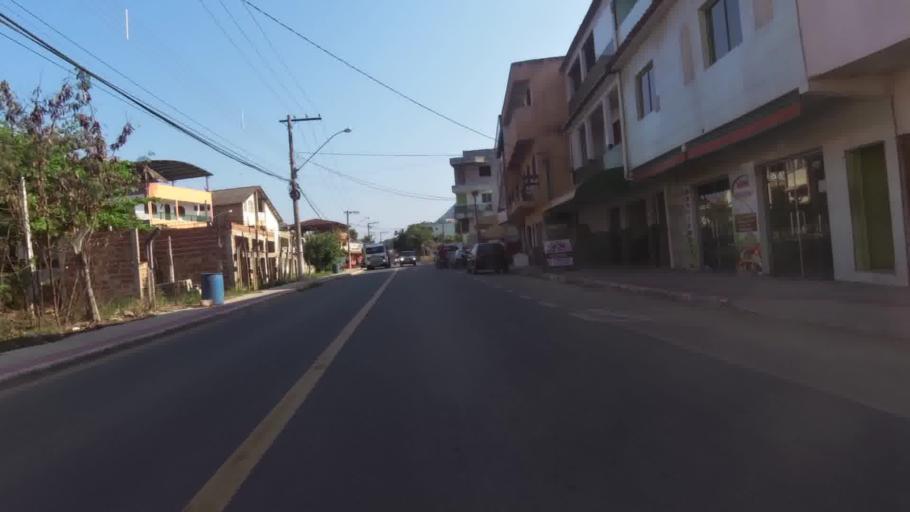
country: BR
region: Espirito Santo
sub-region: Piuma
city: Piuma
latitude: -20.8500
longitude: -40.7486
